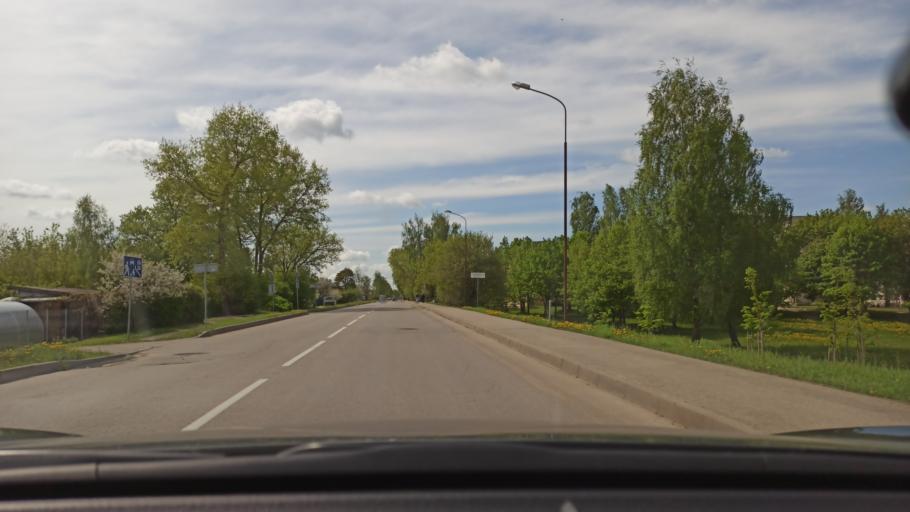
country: LT
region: Siauliu apskritis
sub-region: Siauliai
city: Siauliai
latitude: 55.9146
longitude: 23.3587
